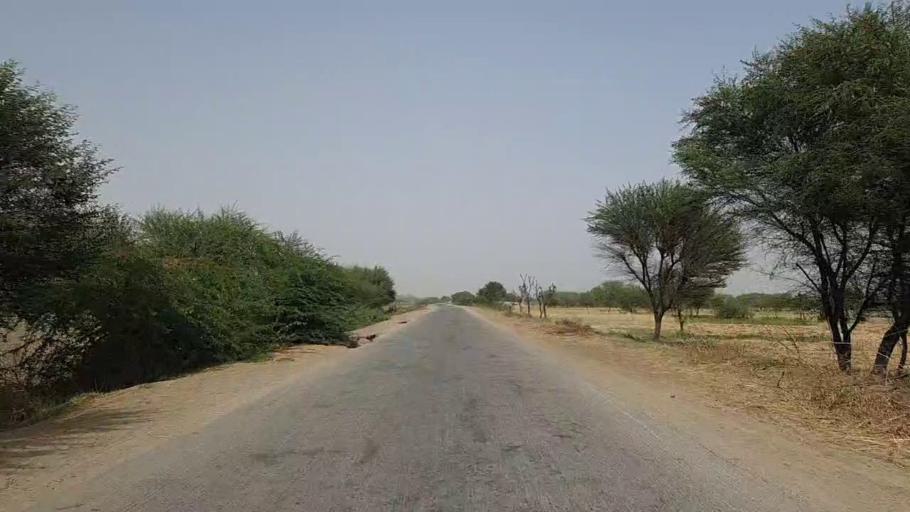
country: PK
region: Sindh
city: Tando Bago
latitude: 24.9118
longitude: 69.0945
